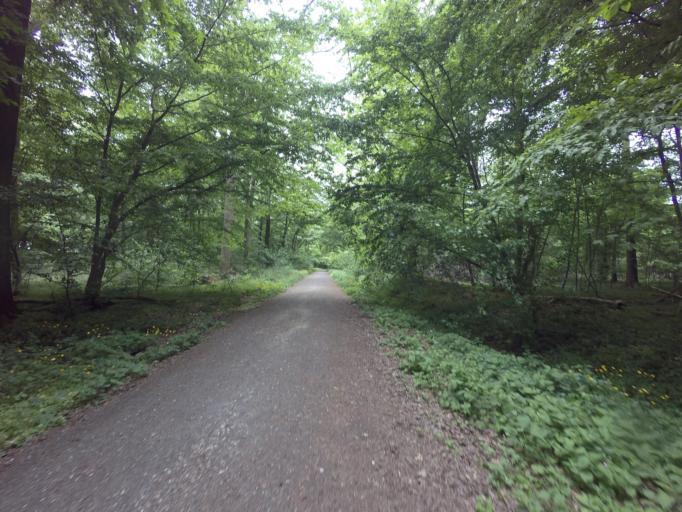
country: DE
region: Lower Saxony
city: Cremlingen
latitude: 52.2522
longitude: 10.6030
